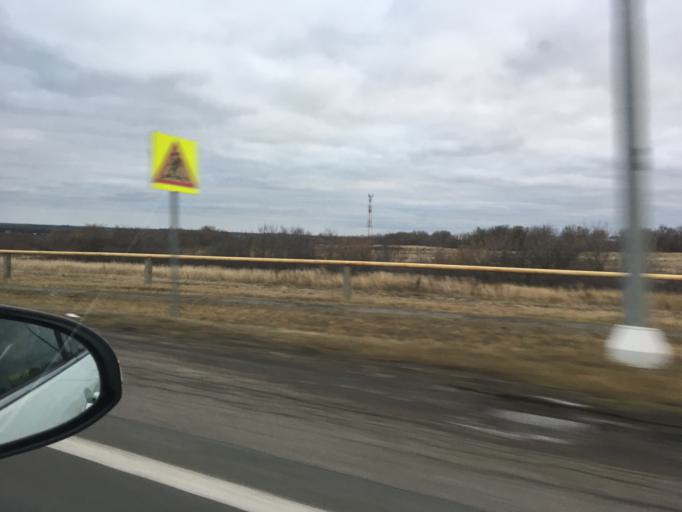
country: RU
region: Saratov
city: Samoylovka
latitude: 51.4885
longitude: 43.9258
